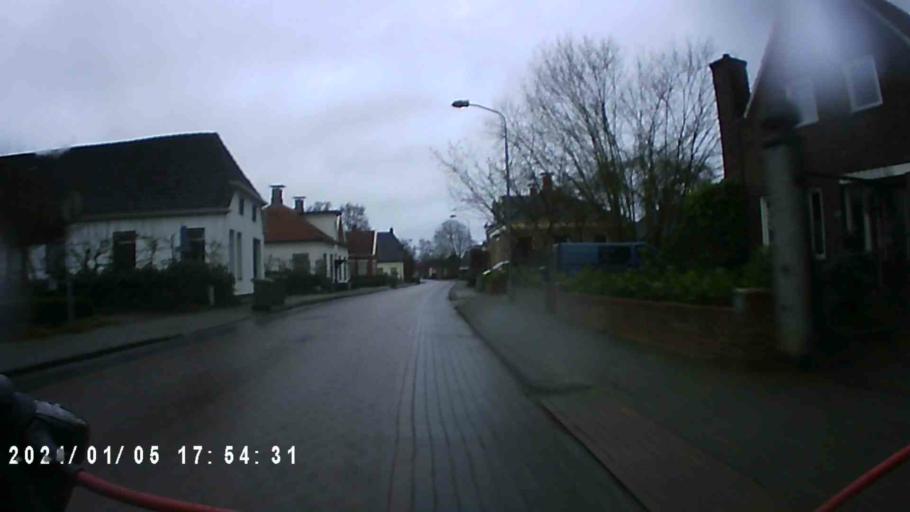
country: NL
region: Groningen
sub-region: Gemeente Slochteren
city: Slochteren
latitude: 53.2023
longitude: 6.8732
